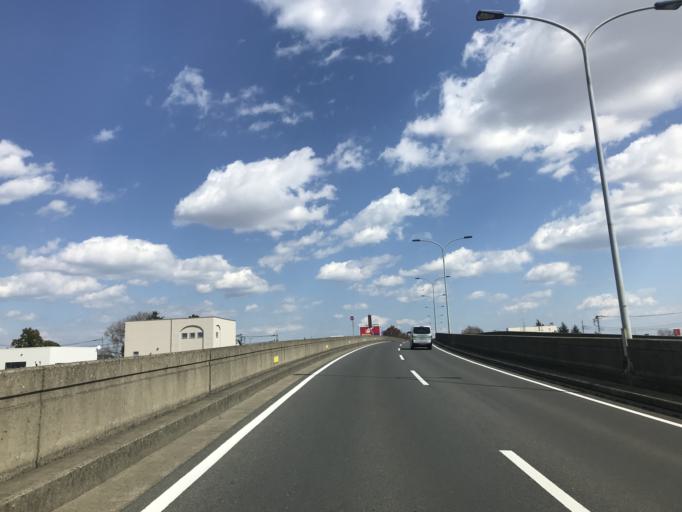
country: JP
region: Ibaraki
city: Mito-shi
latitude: 36.3477
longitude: 140.4623
